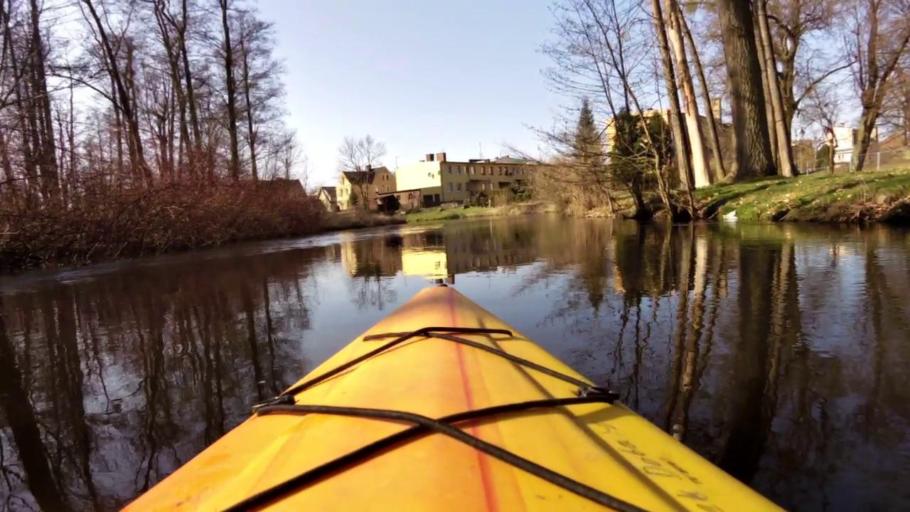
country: PL
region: West Pomeranian Voivodeship
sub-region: Powiat lobeski
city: Resko
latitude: 53.7706
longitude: 15.4055
